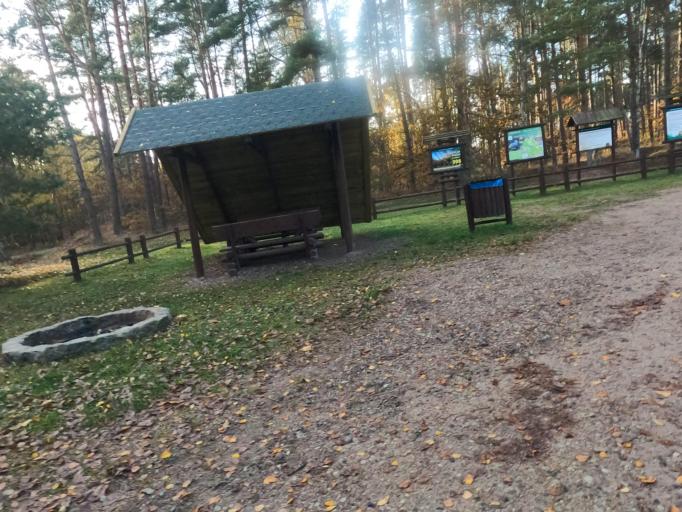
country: PL
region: West Pomeranian Voivodeship
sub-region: Powiat szczecinecki
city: Borne Sulinowo
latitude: 53.5303
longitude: 16.4889
